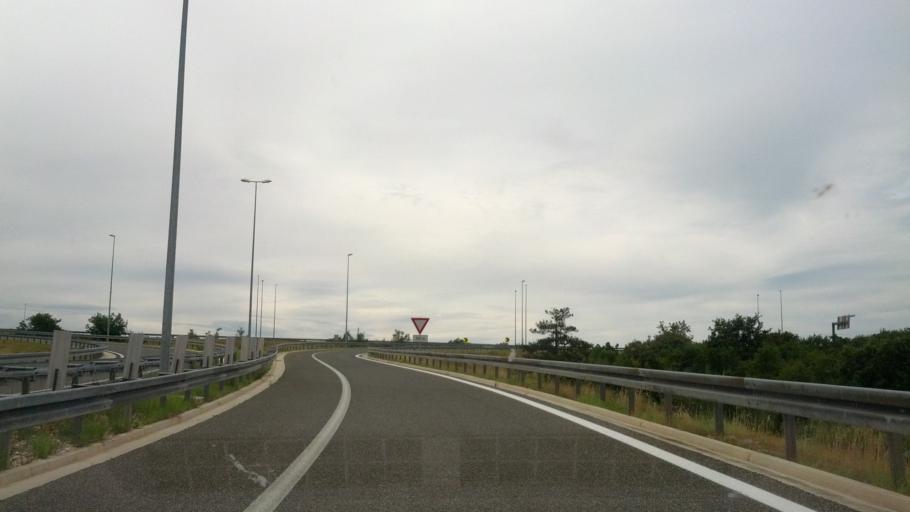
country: HR
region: Istarska
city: Vodnjan
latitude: 45.1129
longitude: 13.8105
